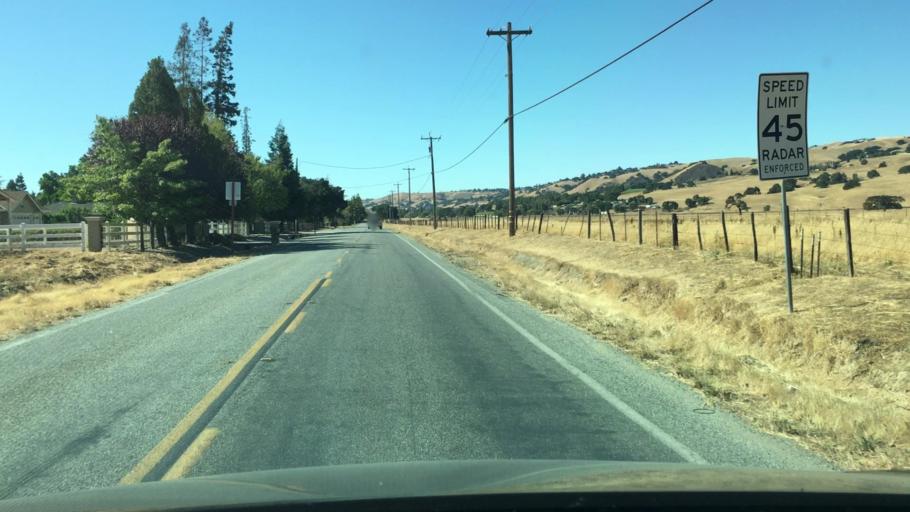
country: US
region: California
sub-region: Santa Clara County
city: San Martin
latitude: 37.0953
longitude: -121.5818
